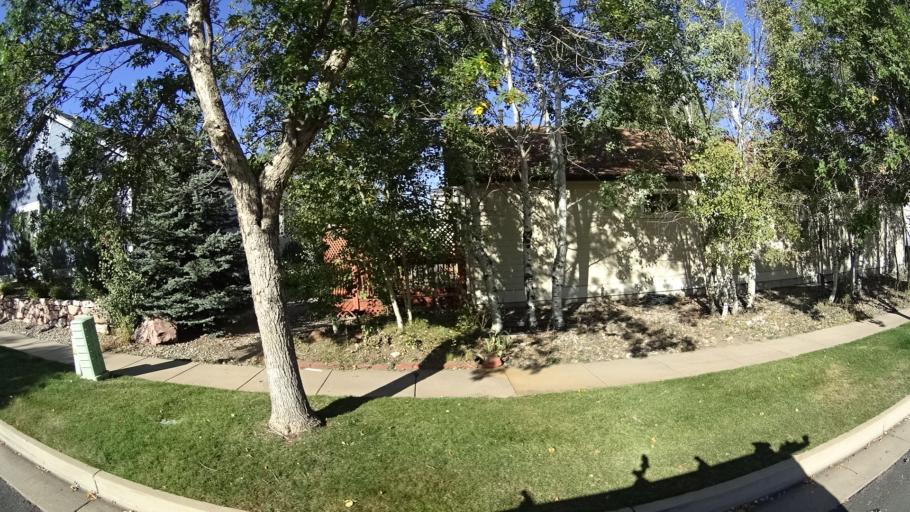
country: US
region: Colorado
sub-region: El Paso County
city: Cimarron Hills
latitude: 38.8765
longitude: -104.6988
